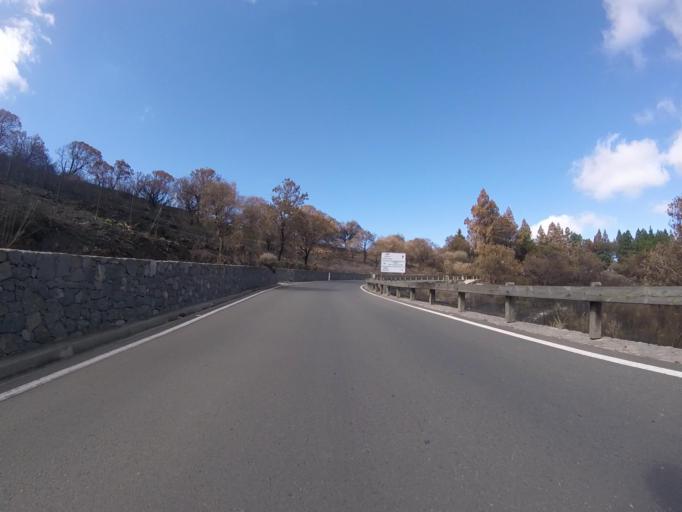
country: ES
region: Canary Islands
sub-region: Provincia de Las Palmas
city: Tejeda
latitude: 28.0053
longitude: -15.5979
